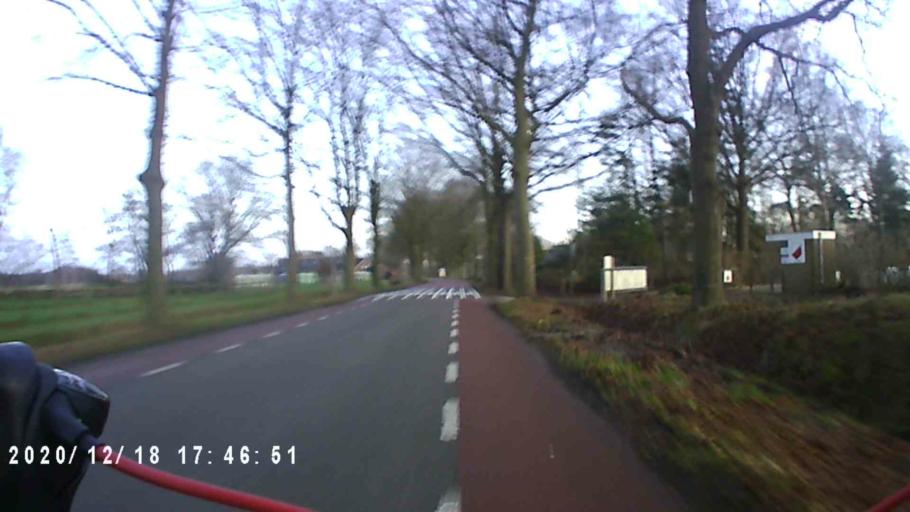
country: NL
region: Drenthe
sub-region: Gemeente Tynaarlo
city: Vries
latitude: 53.1114
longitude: 6.5755
